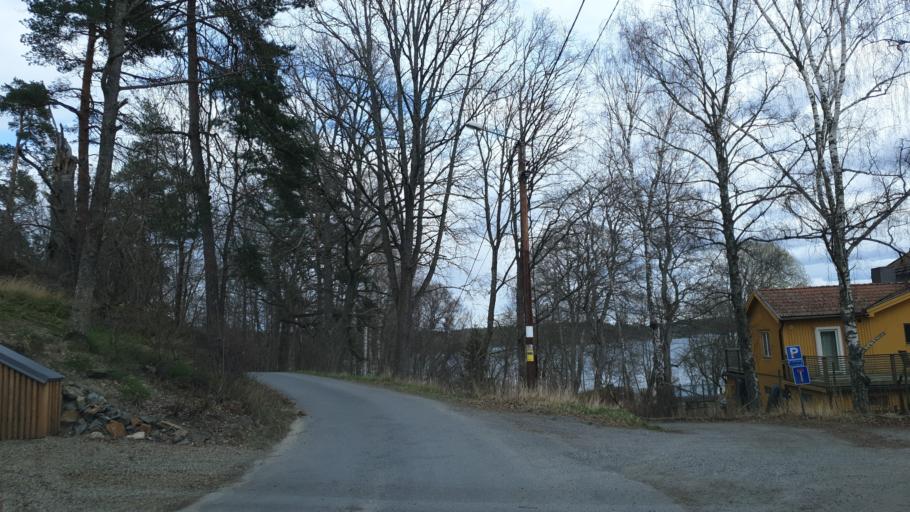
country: SE
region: Stockholm
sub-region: Nacka Kommun
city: Boo
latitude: 59.3215
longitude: 18.3080
